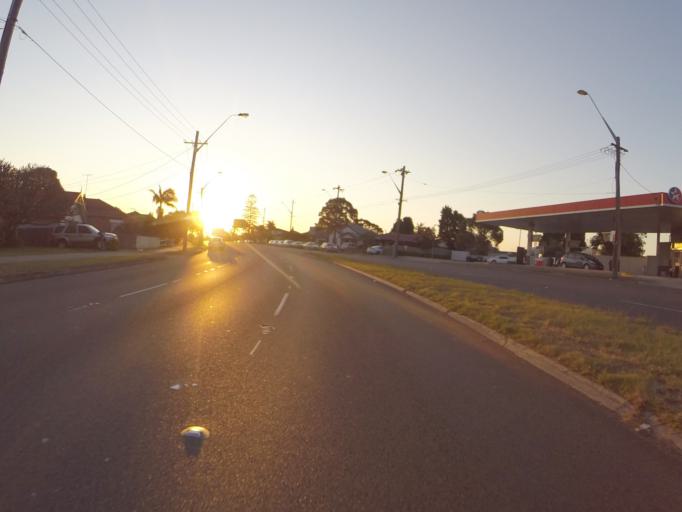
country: AU
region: New South Wales
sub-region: Hurstville
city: Penshurst
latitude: -33.9578
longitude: 151.0684
